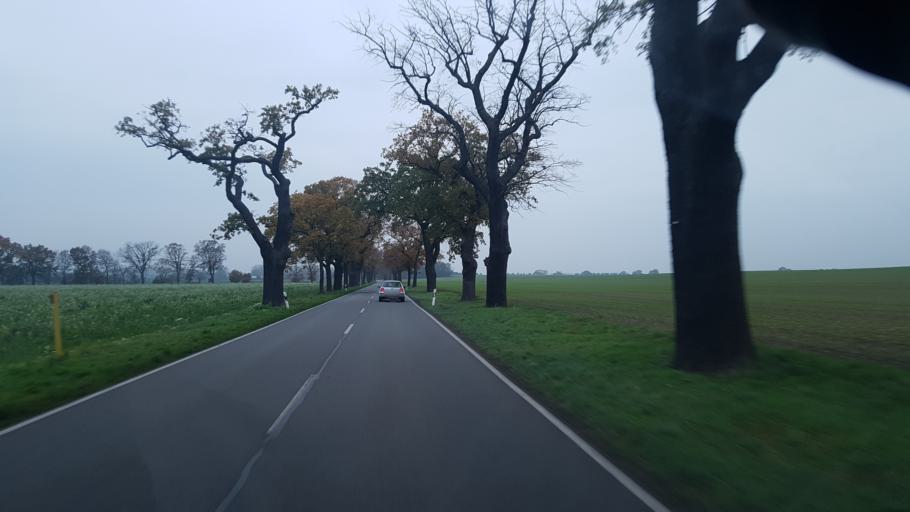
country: DE
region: Brandenburg
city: Fehrbellin
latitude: 52.8419
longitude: 12.8297
